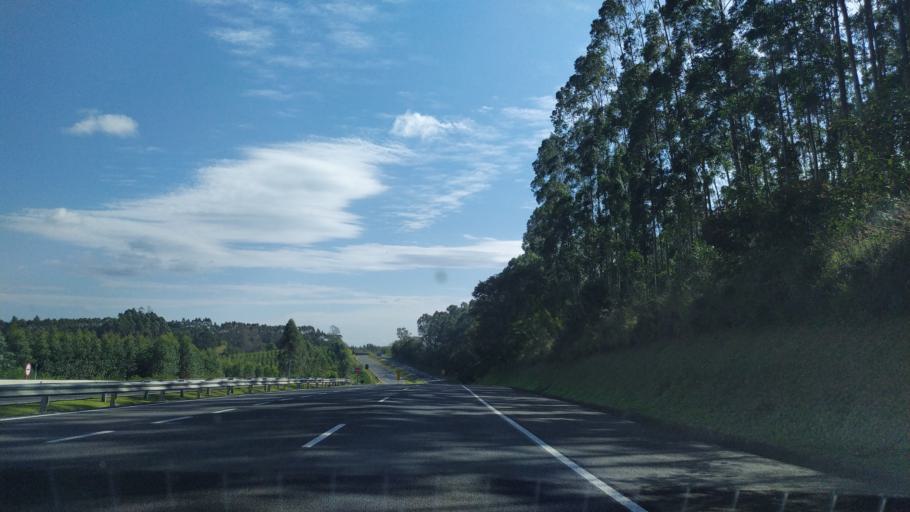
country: BR
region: Parana
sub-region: Telemaco Borba
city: Telemaco Borba
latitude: -24.4242
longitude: -50.7708
